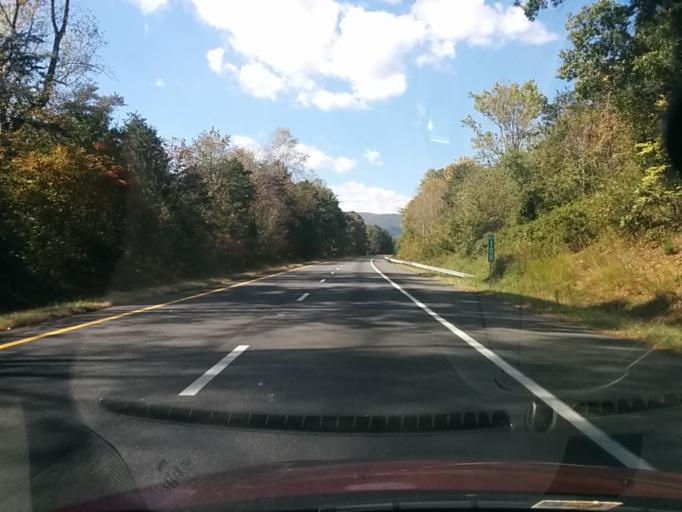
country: US
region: Virginia
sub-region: Albemarle County
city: Crozet
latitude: 38.0410
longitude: -78.7166
